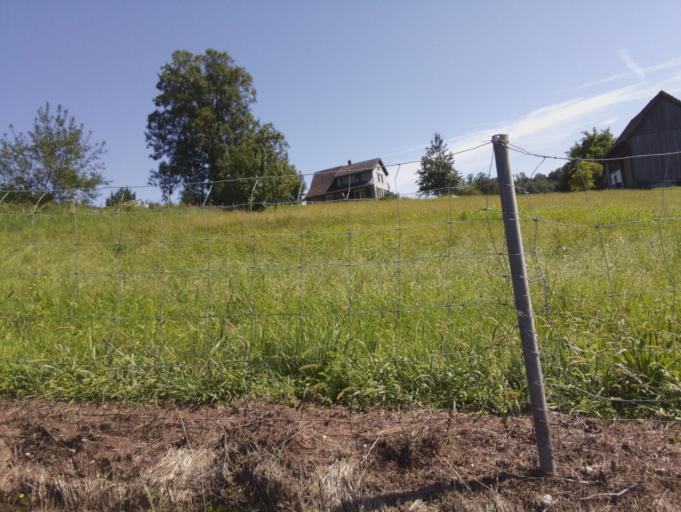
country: CH
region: Schwyz
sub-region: Bezirk March
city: Schubelbach
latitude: 47.1932
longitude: 8.9128
